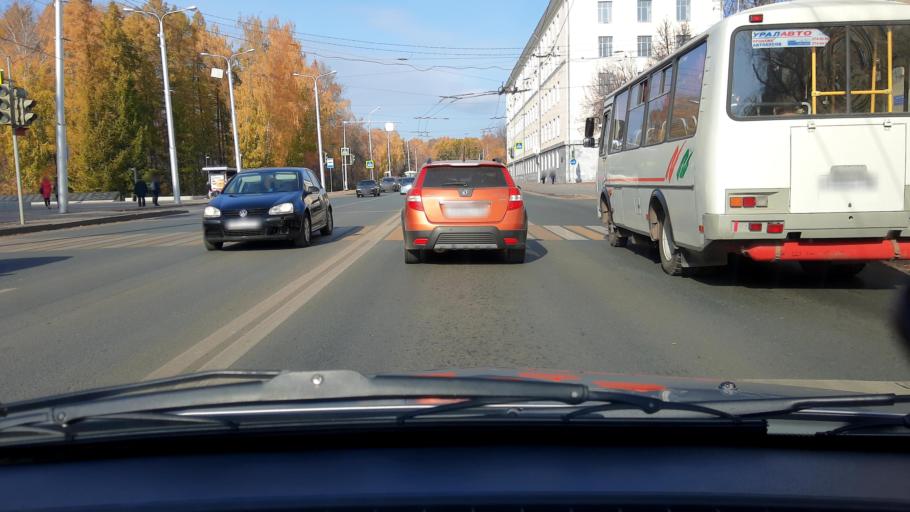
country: RU
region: Bashkortostan
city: Ufa
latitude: 54.8172
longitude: 56.0578
